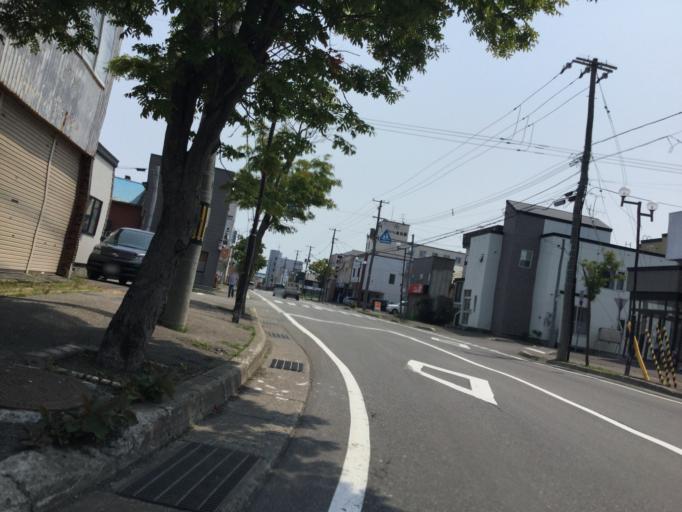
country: JP
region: Hokkaido
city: Wakkanai
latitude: 45.3972
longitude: 141.6882
